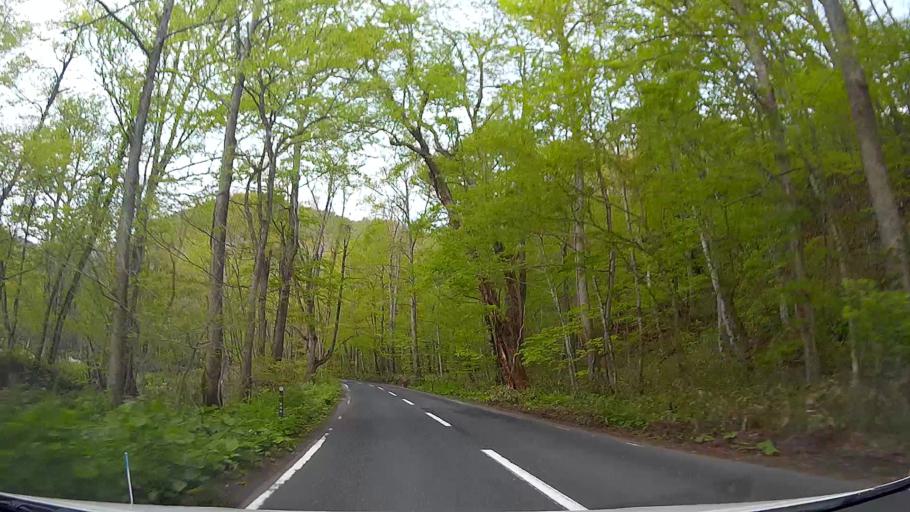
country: JP
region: Aomori
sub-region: Aomori Shi
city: Furudate
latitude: 40.5687
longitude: 140.9780
